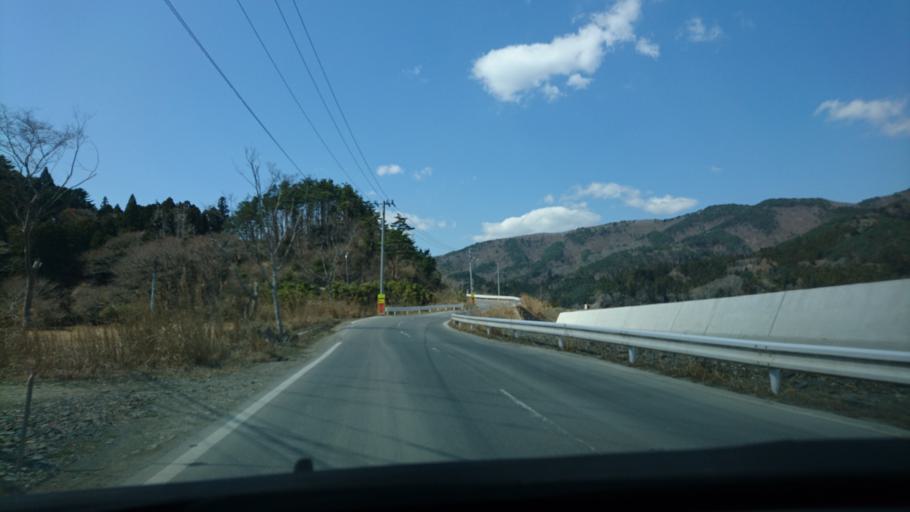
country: JP
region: Miyagi
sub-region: Oshika Gun
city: Onagawa Cho
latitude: 38.5159
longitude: 141.4762
